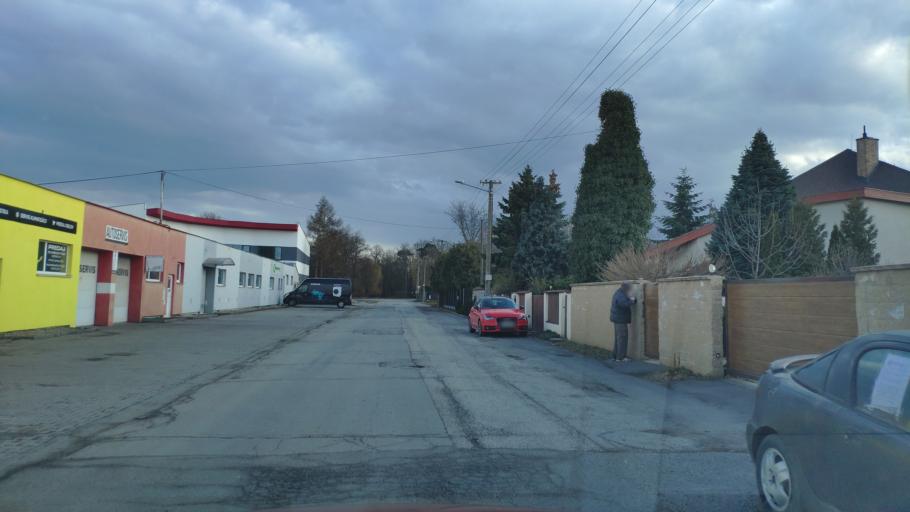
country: SK
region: Kosicky
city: Kosice
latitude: 48.6809
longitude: 21.2664
